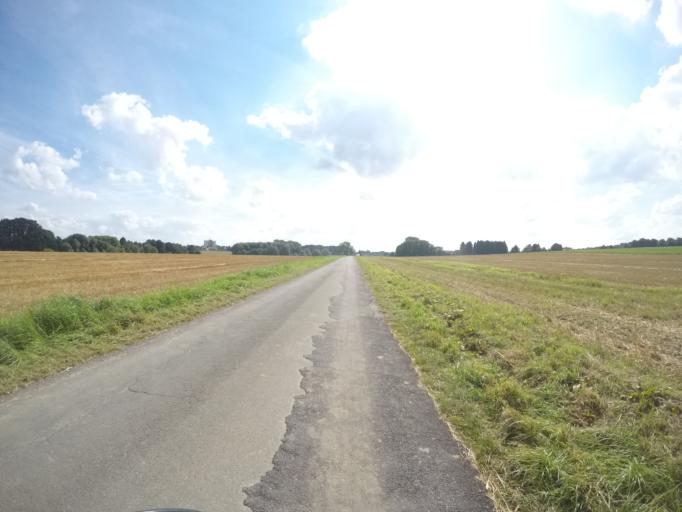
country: DE
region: North Rhine-Westphalia
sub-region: Regierungsbezirk Detmold
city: Bielefeld
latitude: 52.0620
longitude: 8.5941
